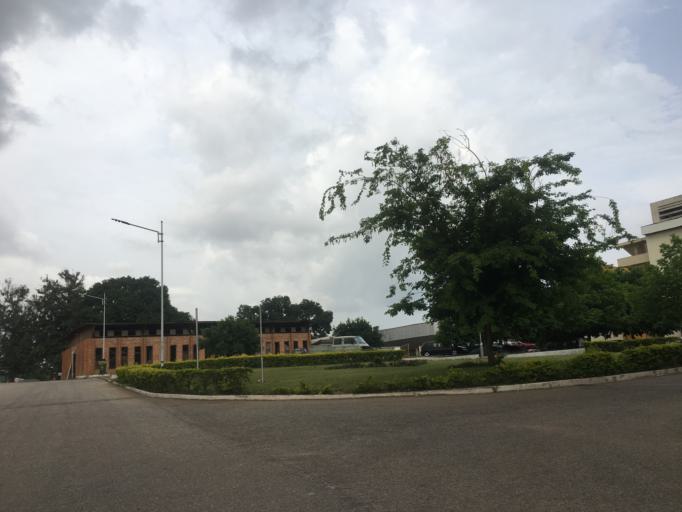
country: GH
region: Ashanti
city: Mamponteng
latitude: 6.6749
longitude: -1.5650
